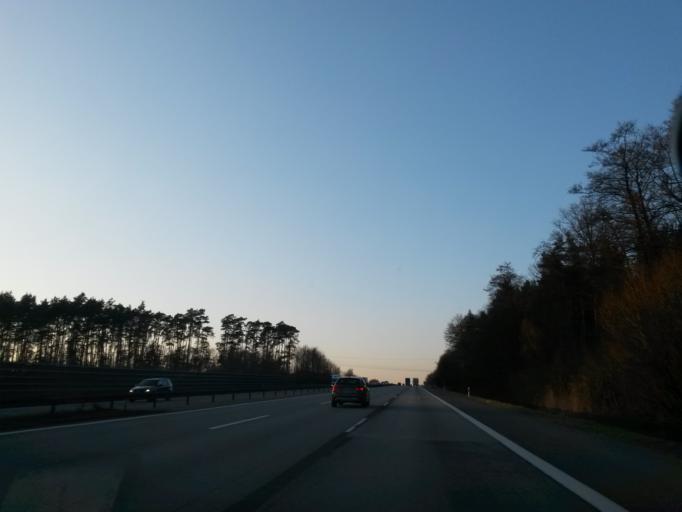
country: DE
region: Bavaria
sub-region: Regierungsbezirk Mittelfranken
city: Allersberg
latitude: 49.2104
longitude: 11.2322
